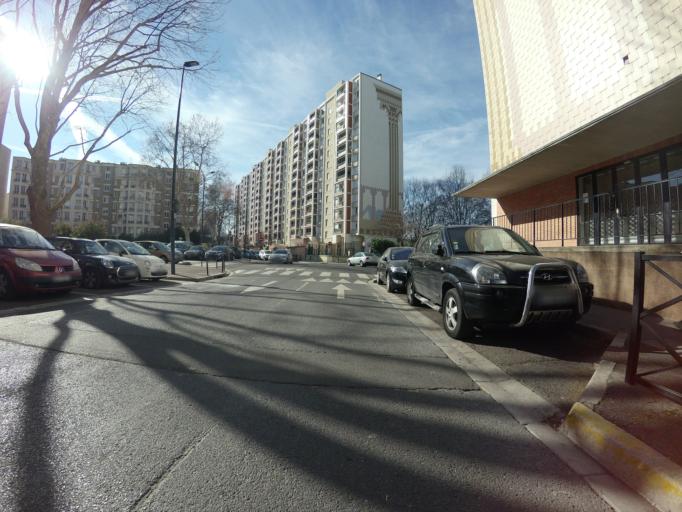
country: FR
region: Ile-de-France
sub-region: Departement des Hauts-de-Seine
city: Clichy
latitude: 48.9090
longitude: 2.3029
